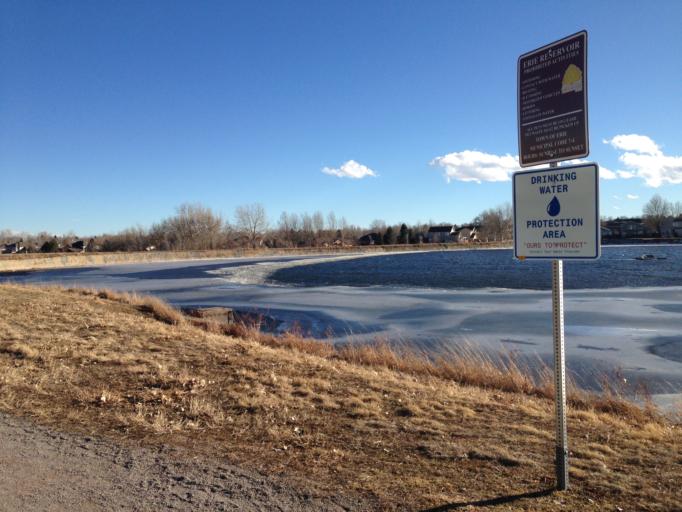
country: US
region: Colorado
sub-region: Boulder County
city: Lafayette
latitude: 40.0197
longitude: -105.0975
